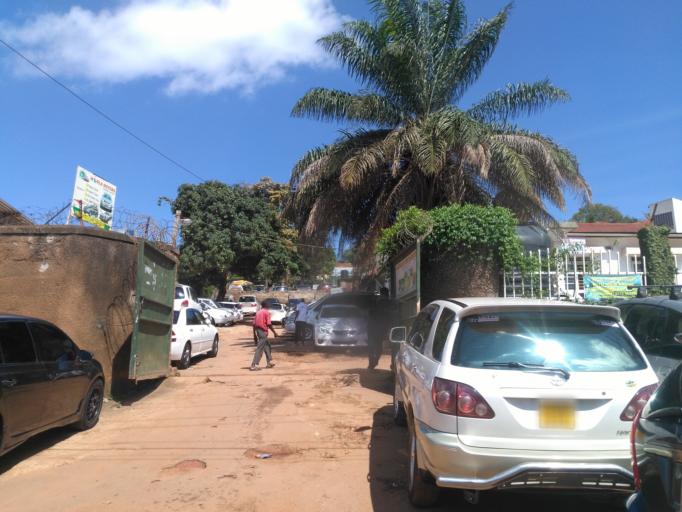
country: UG
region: Central Region
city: Kampala Central Division
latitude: 0.3257
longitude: 32.5760
